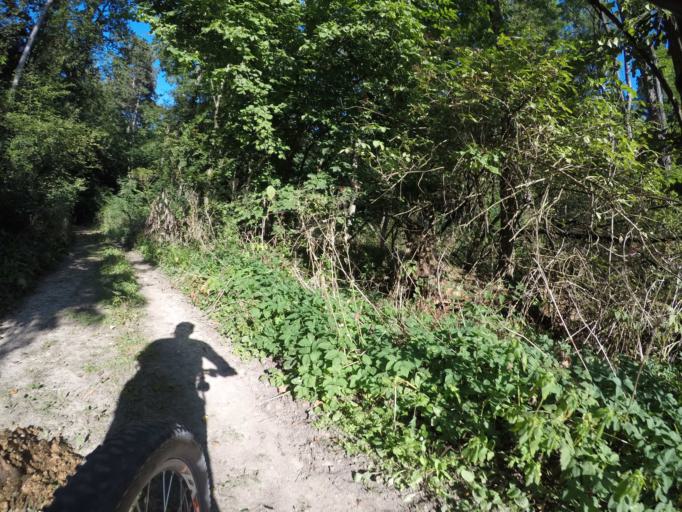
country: AT
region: Lower Austria
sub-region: Politischer Bezirk Bruck an der Leitha
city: Mannersdorf am Leithagebirge
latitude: 47.9590
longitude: 16.6136
